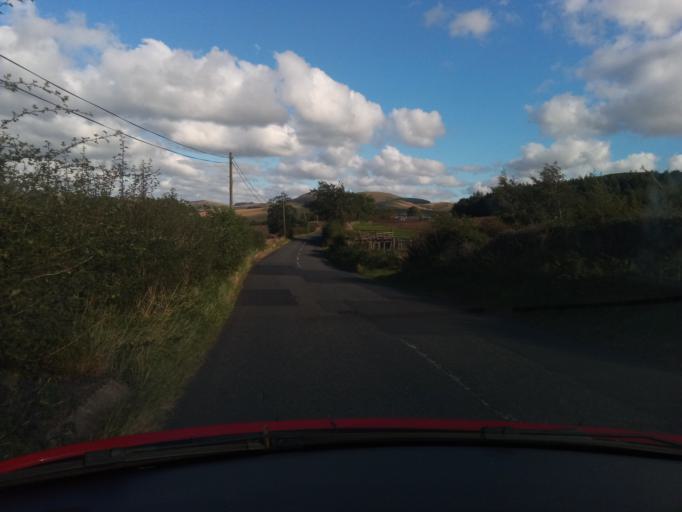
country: GB
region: Scotland
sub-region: The Scottish Borders
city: Coldstream
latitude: 55.5476
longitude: -2.2949
